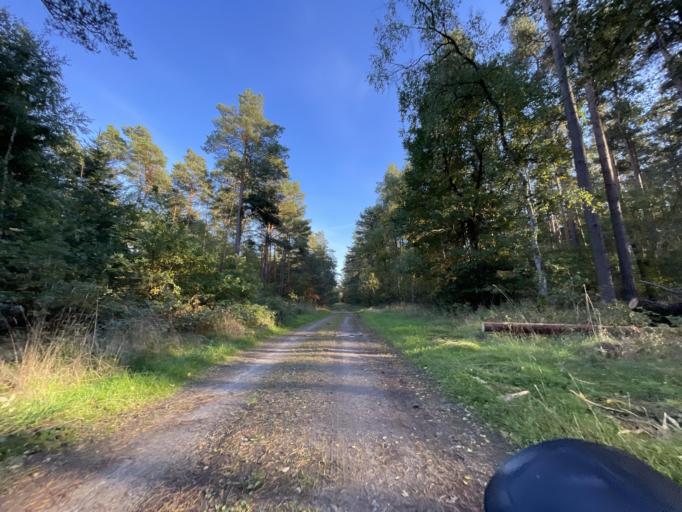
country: DE
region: Lower Saxony
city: Barendorf
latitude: 53.2054
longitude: 10.5056
